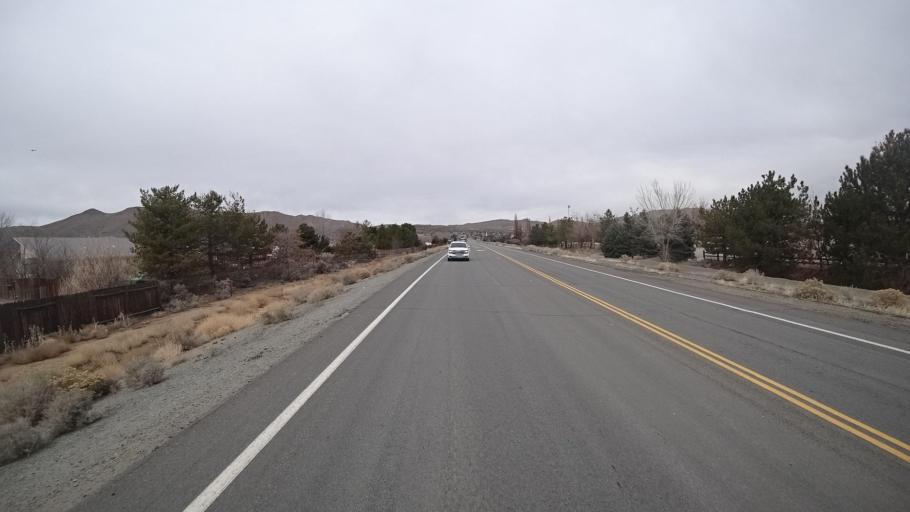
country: US
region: Nevada
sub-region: Washoe County
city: Spanish Springs
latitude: 39.6434
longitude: -119.7211
